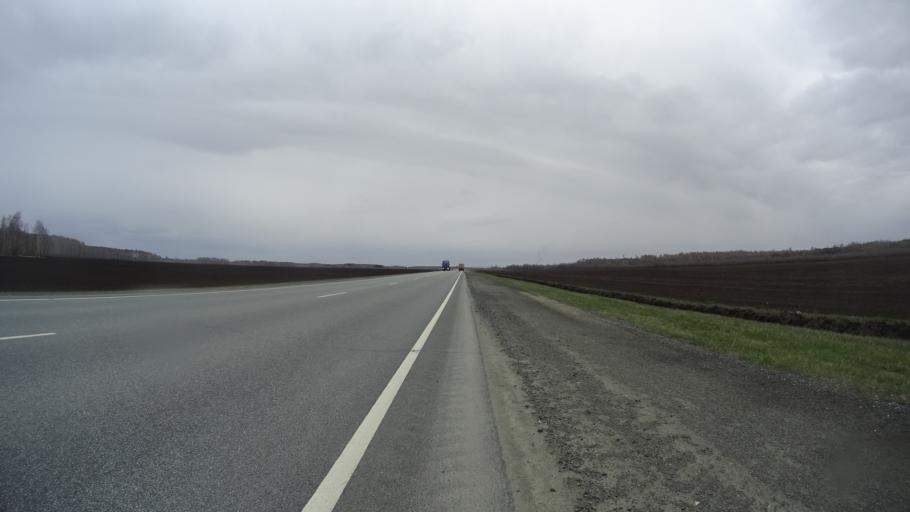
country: RU
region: Chelyabinsk
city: Krasnogorskiy
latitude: 54.5744
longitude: 61.2911
